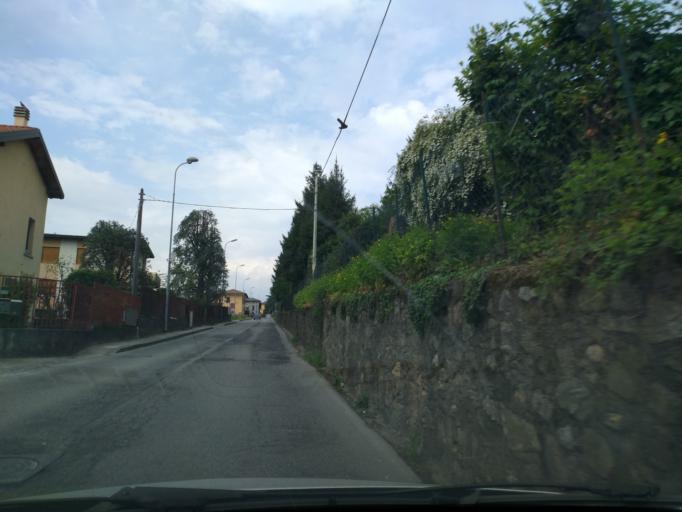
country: IT
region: Lombardy
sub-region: Provincia di Como
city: Alzate Brianza
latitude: 45.7626
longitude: 9.1802
